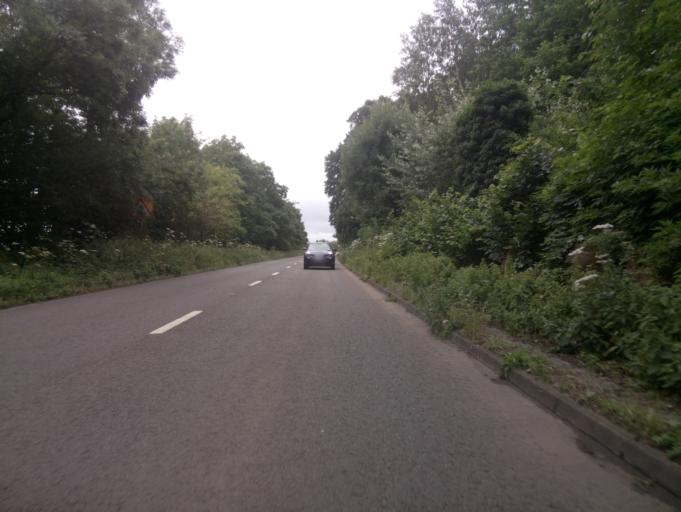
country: GB
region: England
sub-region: Gloucestershire
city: Tewkesbury
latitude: 52.0269
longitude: -2.1630
